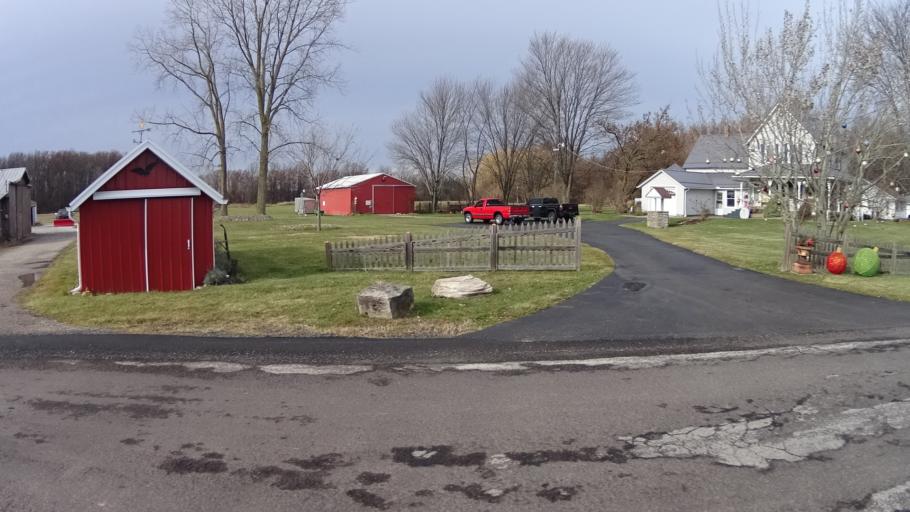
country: US
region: Ohio
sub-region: Lorain County
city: North Ridgeville
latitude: 41.3616
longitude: -82.0566
